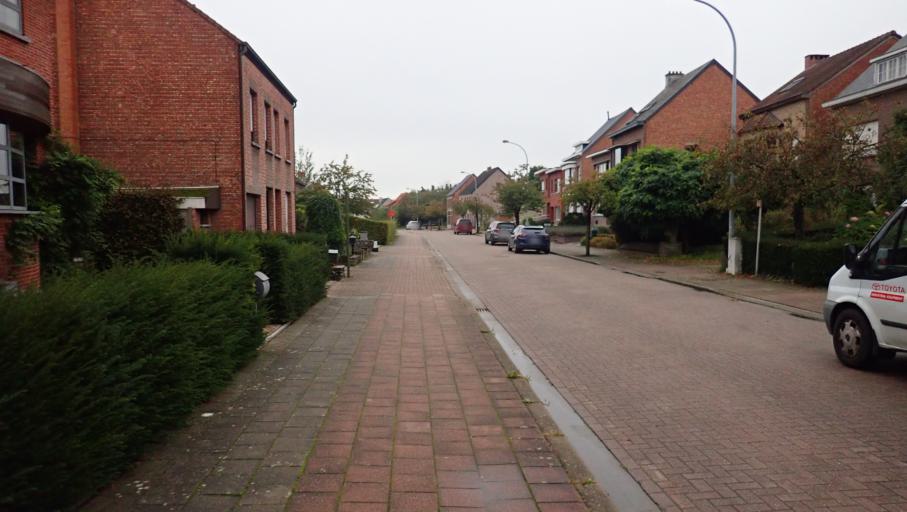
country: BE
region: Flanders
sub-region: Provincie Antwerpen
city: Berlaar
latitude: 51.1161
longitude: 4.6584
